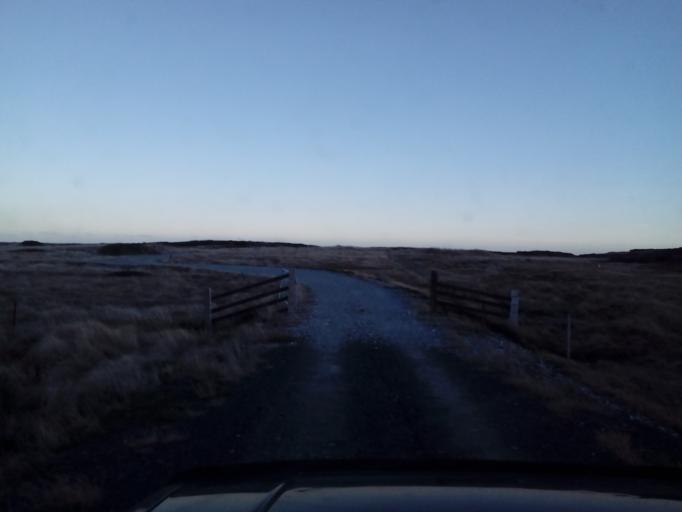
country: FK
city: Stanley
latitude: -51.7015
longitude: -57.8423
